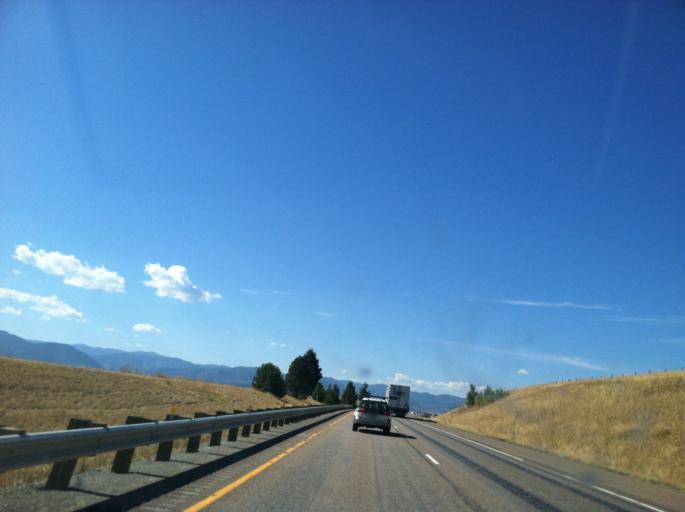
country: US
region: Montana
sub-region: Missoula County
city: Orchard Homes
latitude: 46.9387
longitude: -114.1041
